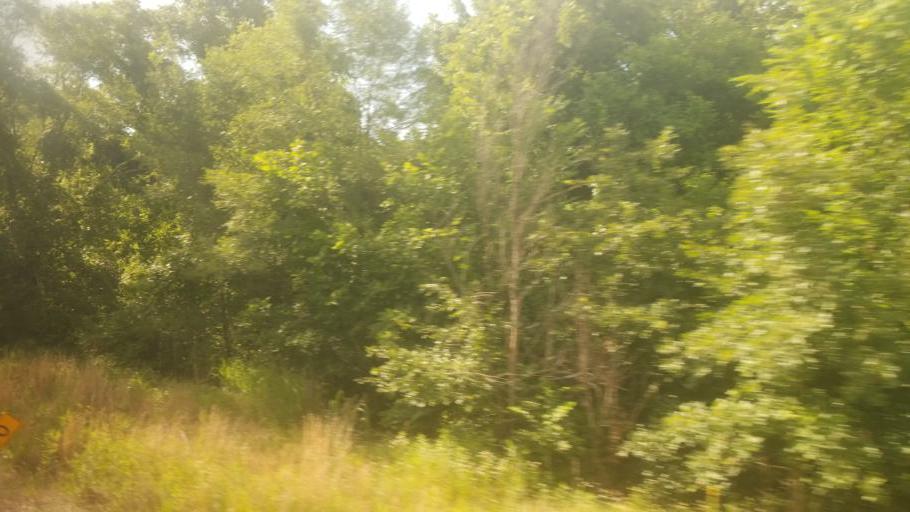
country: US
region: Kansas
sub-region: Wyandotte County
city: Edwardsville
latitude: 39.0501
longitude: -94.8457
